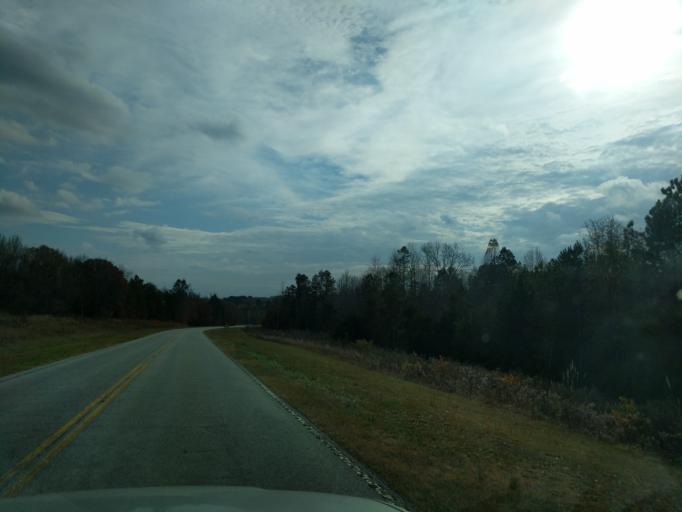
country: US
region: Georgia
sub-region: Franklin County
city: Gumlog
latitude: 34.5733
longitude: -83.0494
